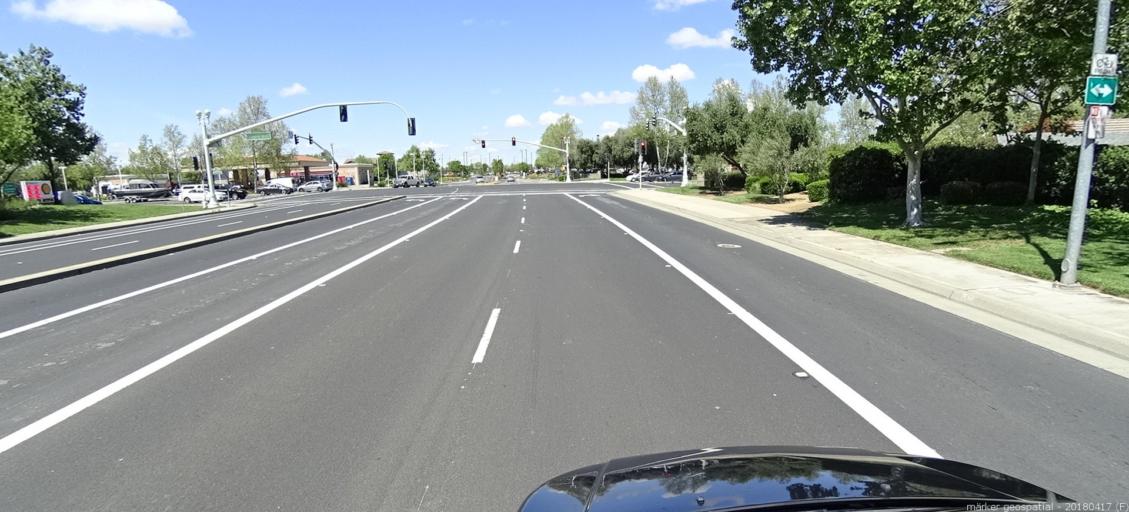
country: US
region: California
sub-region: Sacramento County
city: Laguna
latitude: 38.4272
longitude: -121.4806
